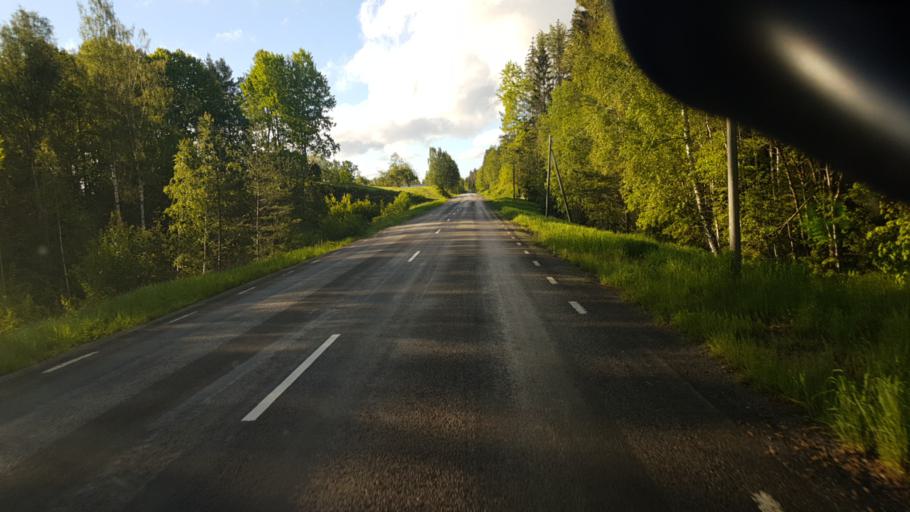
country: SE
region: Vaermland
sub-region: Arvika Kommun
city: Arvika
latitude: 59.6247
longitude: 12.5019
